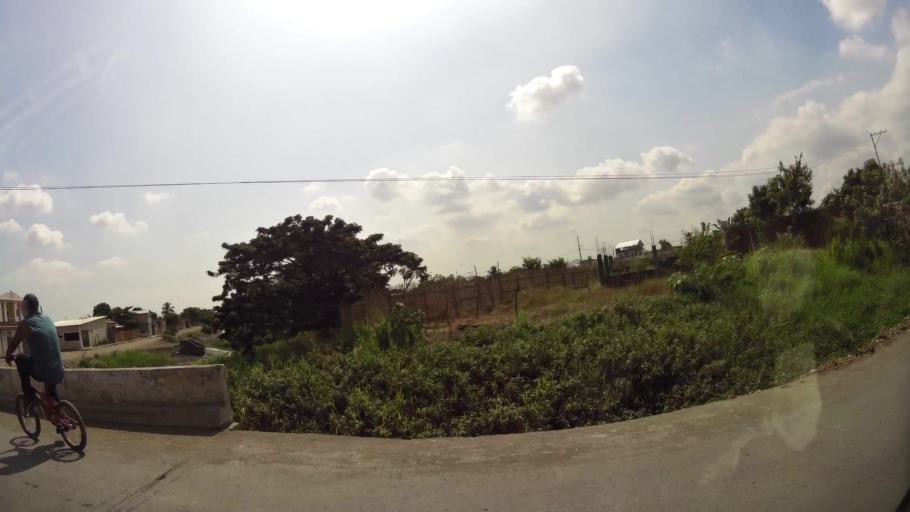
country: EC
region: Guayas
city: Eloy Alfaro
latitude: -2.1504
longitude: -79.8287
